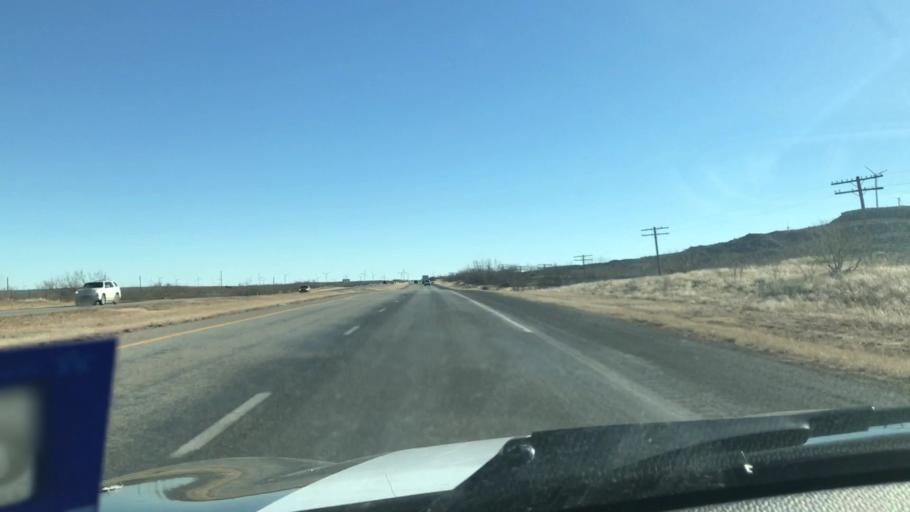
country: US
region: Texas
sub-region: Scurry County
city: Snyder
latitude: 32.9693
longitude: -101.0978
